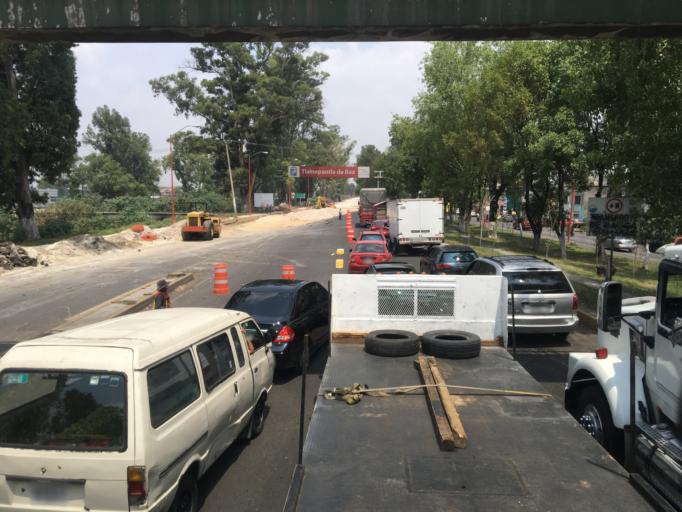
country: MX
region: Mexico
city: Tlalnepantla
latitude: 19.5279
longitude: -99.1618
